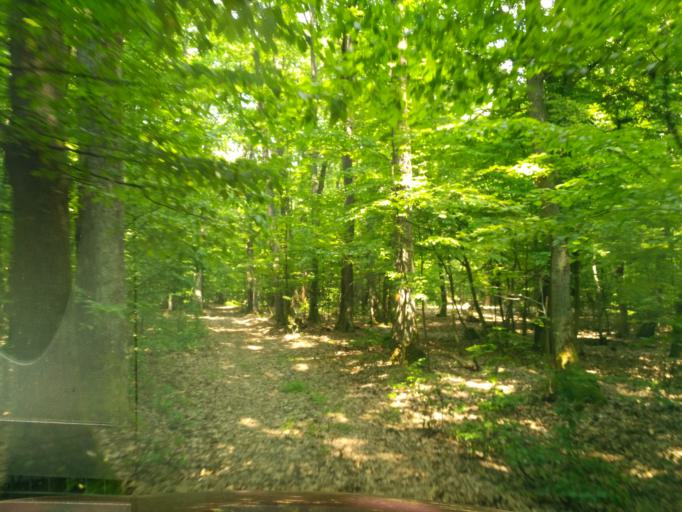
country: SK
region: Kosicky
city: Moldava nad Bodvou
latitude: 48.6488
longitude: 21.0353
